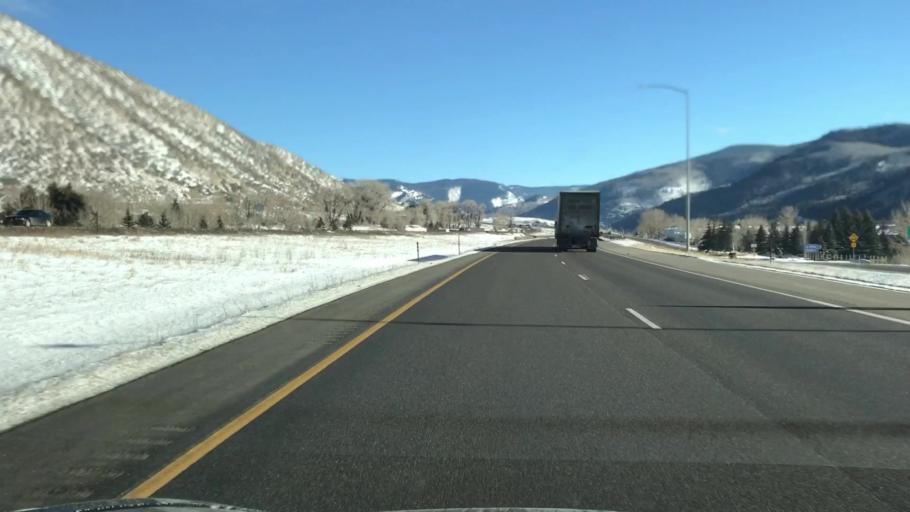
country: US
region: Colorado
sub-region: Eagle County
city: Avon
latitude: 39.6384
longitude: -106.5251
